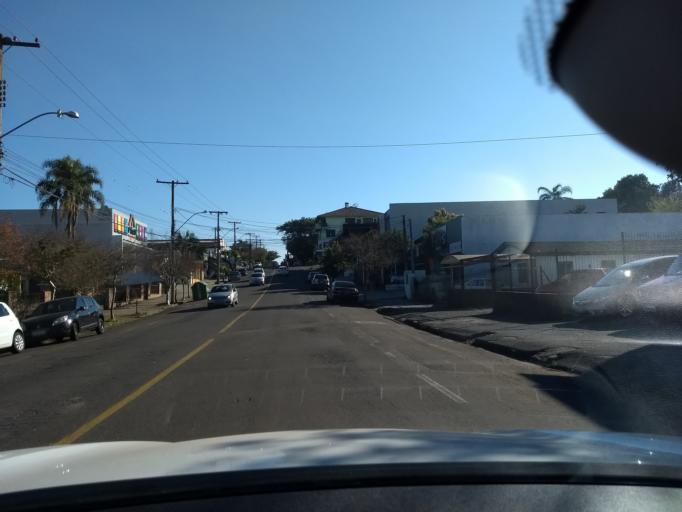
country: BR
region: Rio Grande do Sul
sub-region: Santa Cruz Do Sul
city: Santa Cruz do Sul
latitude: -29.7171
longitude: -52.4415
